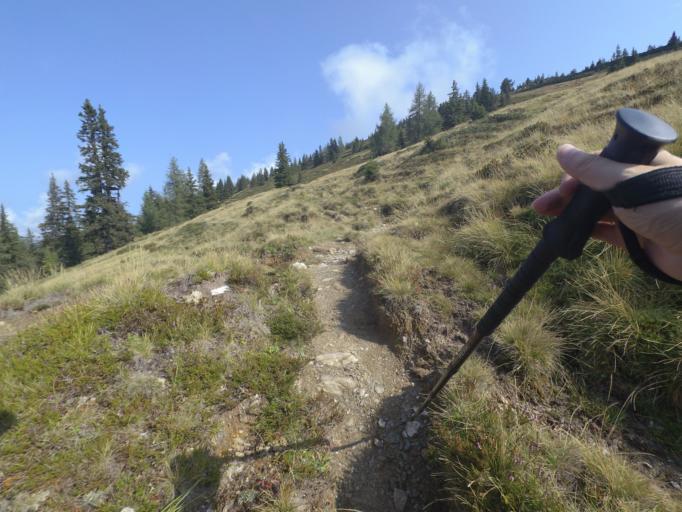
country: AT
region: Salzburg
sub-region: Politischer Bezirk Sankt Johann im Pongau
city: Kleinarl
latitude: 47.2606
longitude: 13.2765
